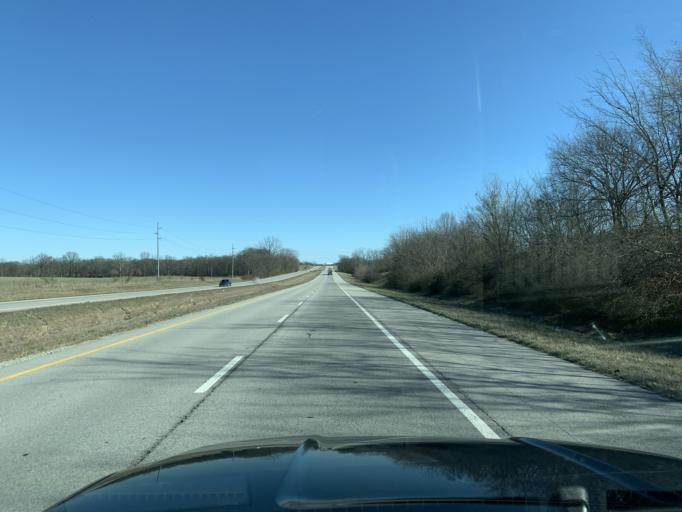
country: US
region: Tennessee
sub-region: Maury County
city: Mount Pleasant
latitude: 35.5536
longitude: -87.2029
